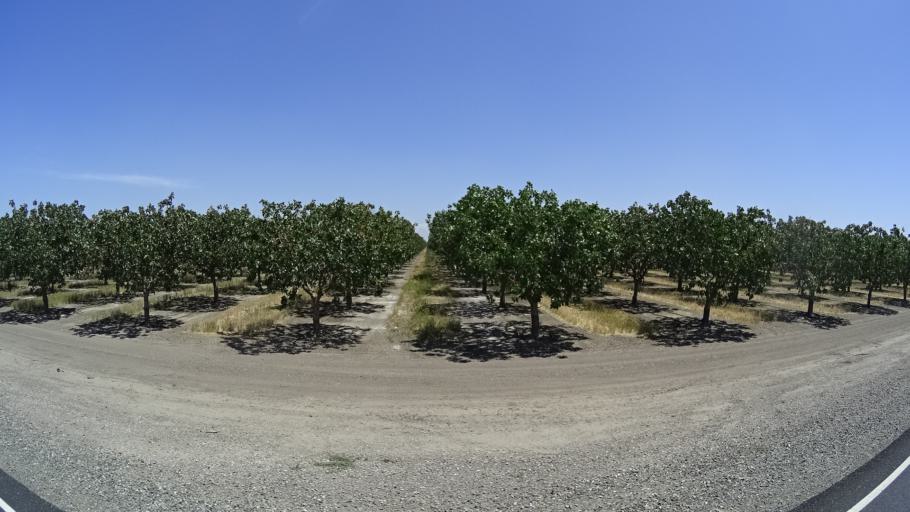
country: US
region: California
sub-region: Kings County
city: Corcoran
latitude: 36.1030
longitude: -119.5364
